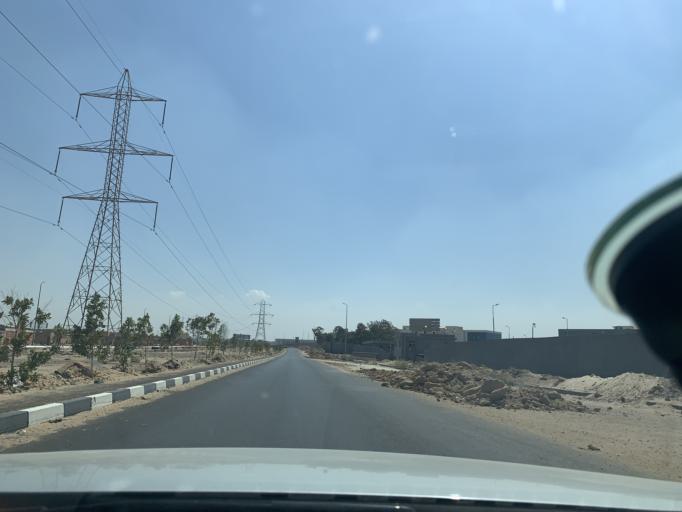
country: EG
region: Muhafazat al Qahirah
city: Cairo
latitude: 30.0307
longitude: 31.3497
